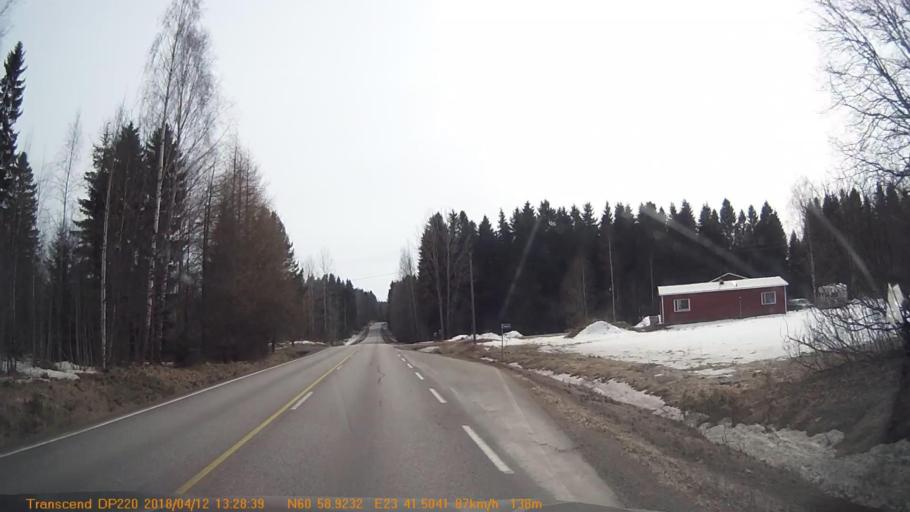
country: FI
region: Pirkanmaa
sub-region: Etelae-Pirkanmaa
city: Kylmaekoski
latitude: 60.9818
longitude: 23.6919
